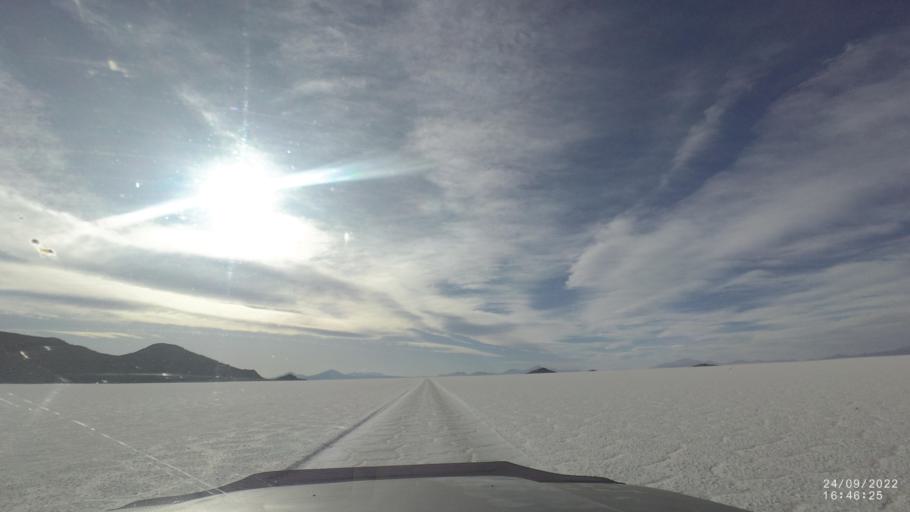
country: BO
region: Potosi
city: Colchani
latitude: -20.1382
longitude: -67.7897
